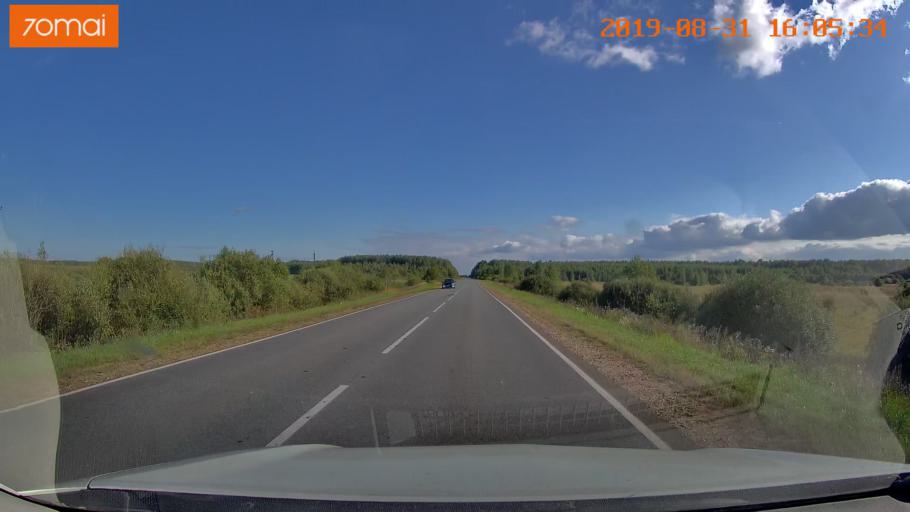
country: RU
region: Kaluga
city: Yukhnov
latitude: 54.6370
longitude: 35.3359
